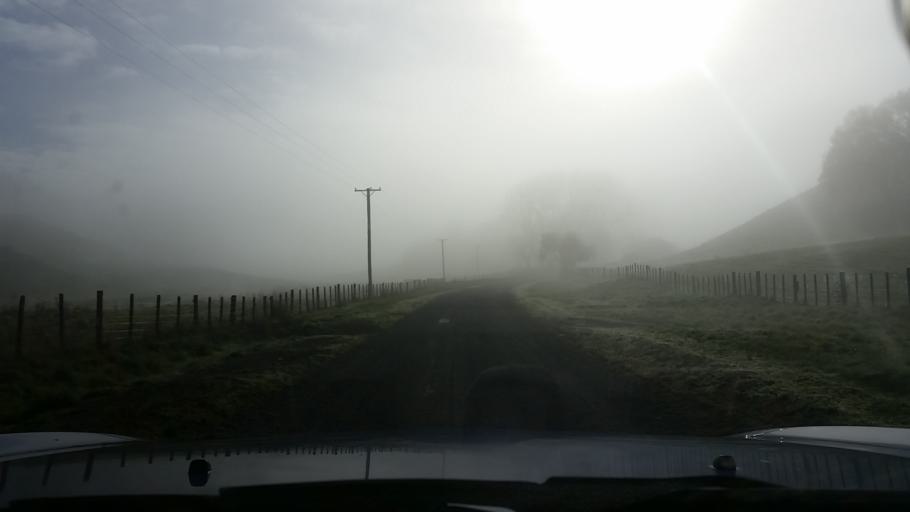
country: NZ
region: Bay of Plenty
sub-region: Rotorua District
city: Rotorua
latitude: -38.3120
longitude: 176.3025
